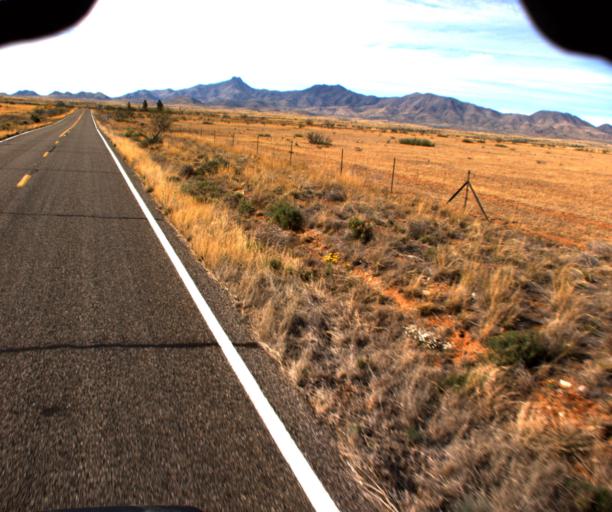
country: US
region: Arizona
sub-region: Cochise County
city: Willcox
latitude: 32.0910
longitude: -109.5316
